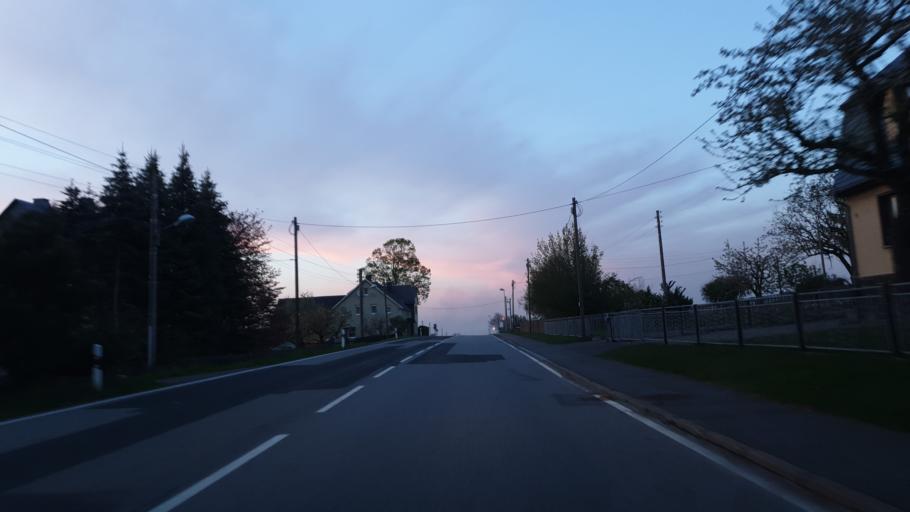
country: DE
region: Saxony
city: Lossnitz
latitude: 50.6584
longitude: 12.7538
